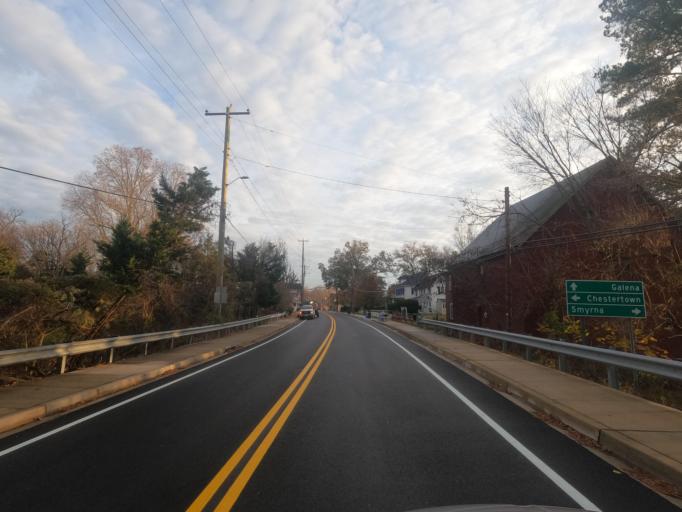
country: US
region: Delaware
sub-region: New Castle County
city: Townsend
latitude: 39.2572
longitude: -75.8387
